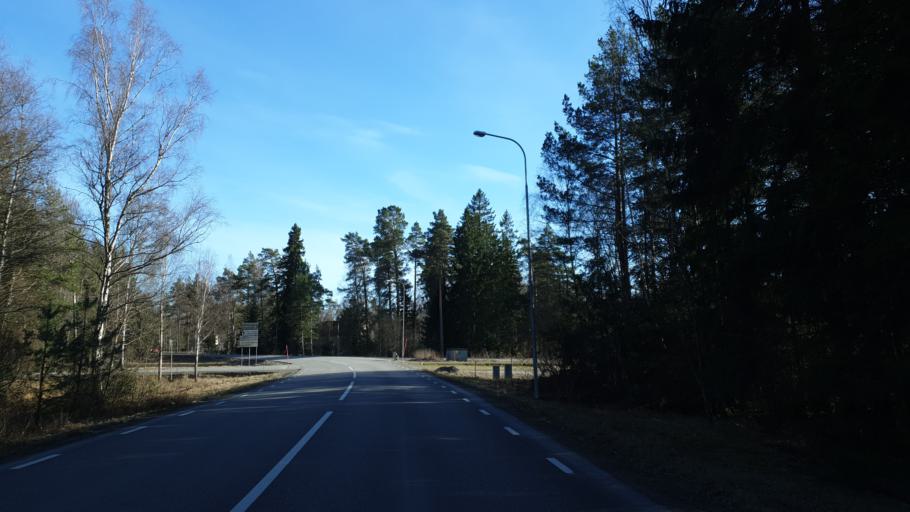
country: SE
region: Vaestra Goetaland
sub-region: Herrljunga Kommun
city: Herrljunga
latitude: 58.0619
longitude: 13.0838
